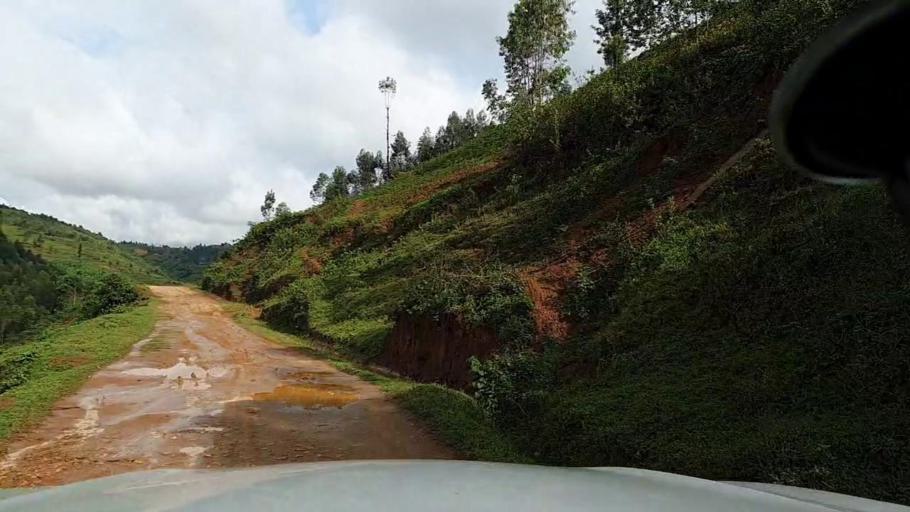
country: RW
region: Western Province
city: Kibuye
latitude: -2.1328
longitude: 29.5006
